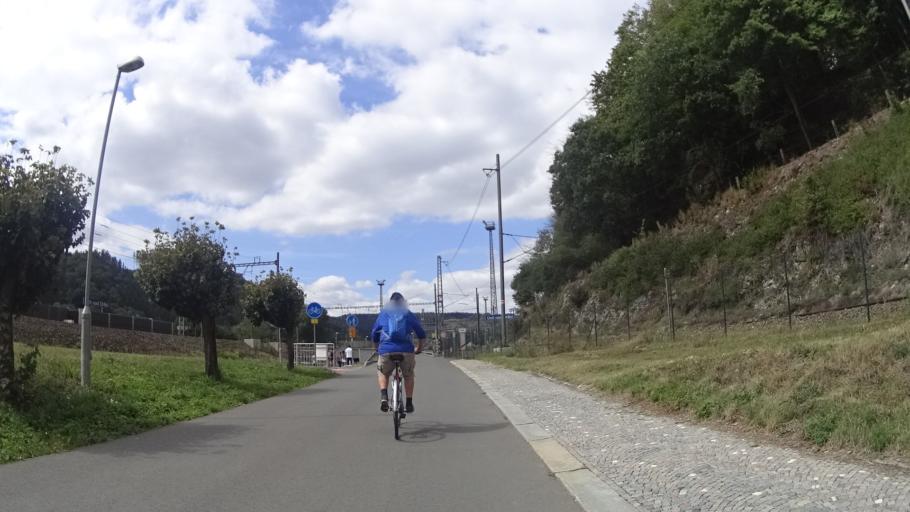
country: CZ
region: Pardubicky
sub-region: Okres Usti nad Orlici
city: Usti nad Orlici
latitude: 49.9716
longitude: 16.3841
